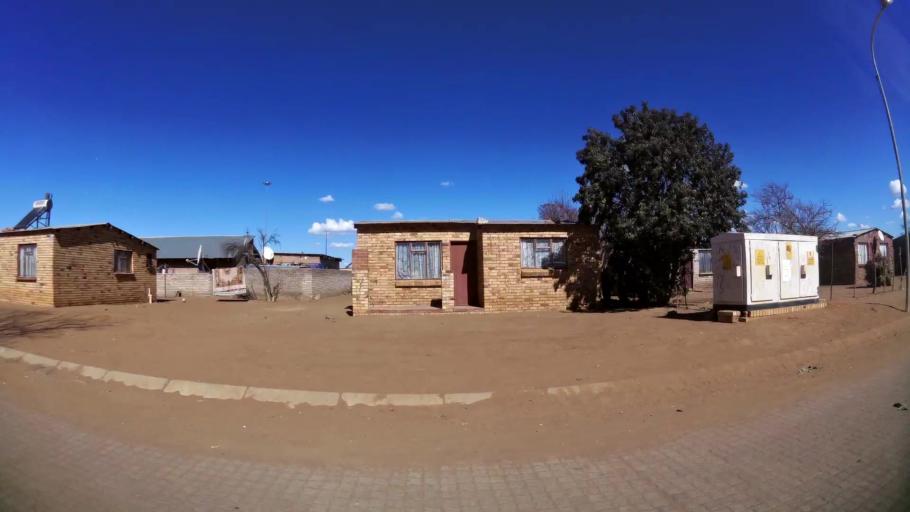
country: ZA
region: North-West
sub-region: Dr Kenneth Kaunda District Municipality
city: Klerksdorp
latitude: -26.8667
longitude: 26.5771
